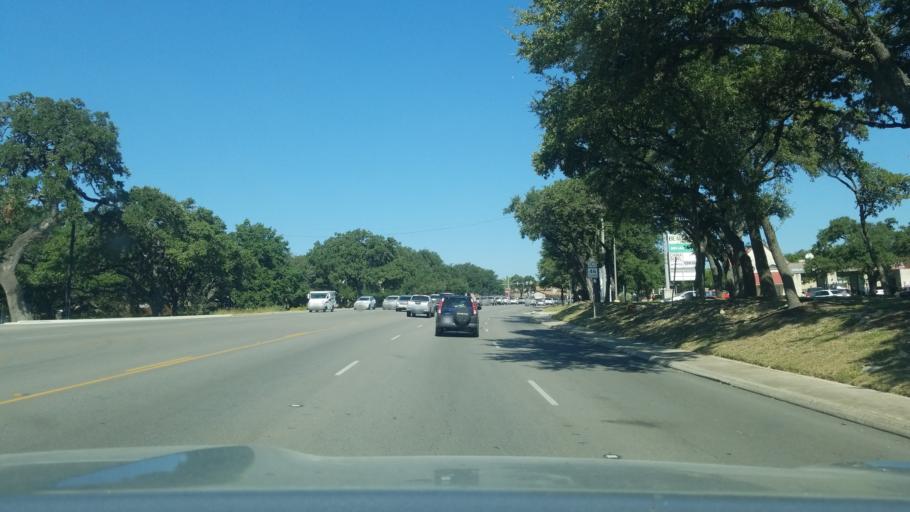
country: US
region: Texas
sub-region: Kendall County
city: Boerne
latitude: 29.7785
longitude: -98.7278
